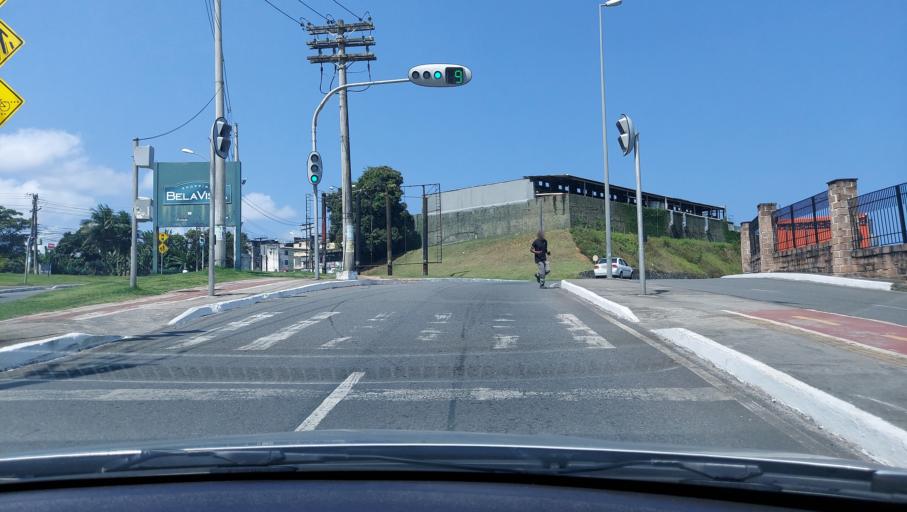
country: BR
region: Bahia
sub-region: Salvador
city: Salvador
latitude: -12.9662
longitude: -38.4739
